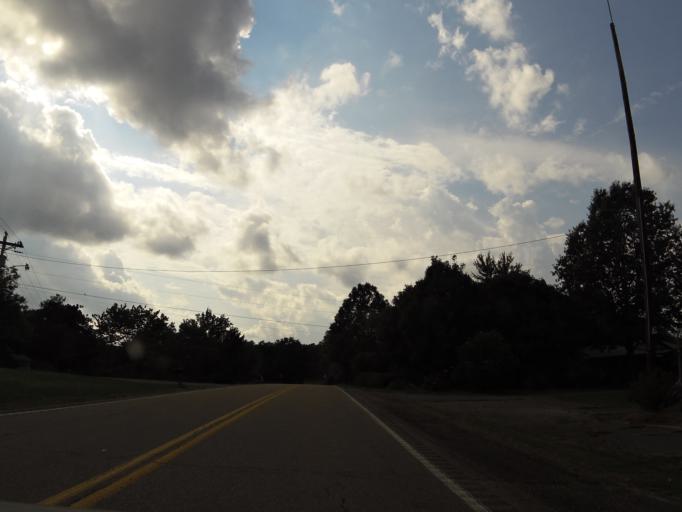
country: US
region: Mississippi
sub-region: Alcorn County
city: Farmington
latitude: 35.0634
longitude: -88.4109
